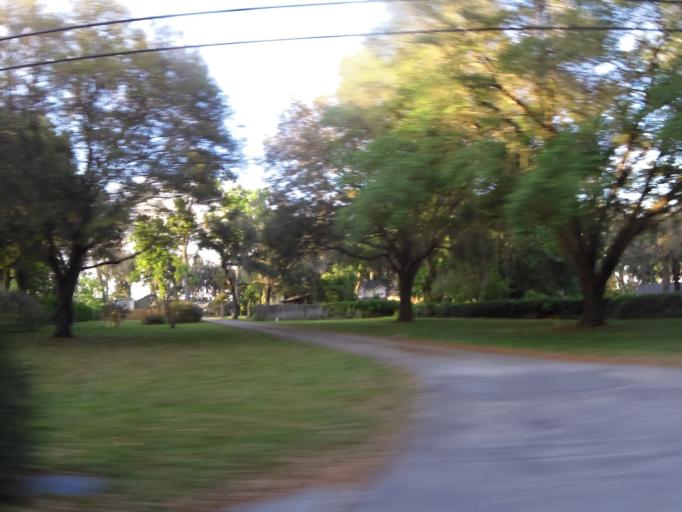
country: US
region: Florida
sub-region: Saint Johns County
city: Fruit Cove
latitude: 30.1269
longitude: -81.5990
